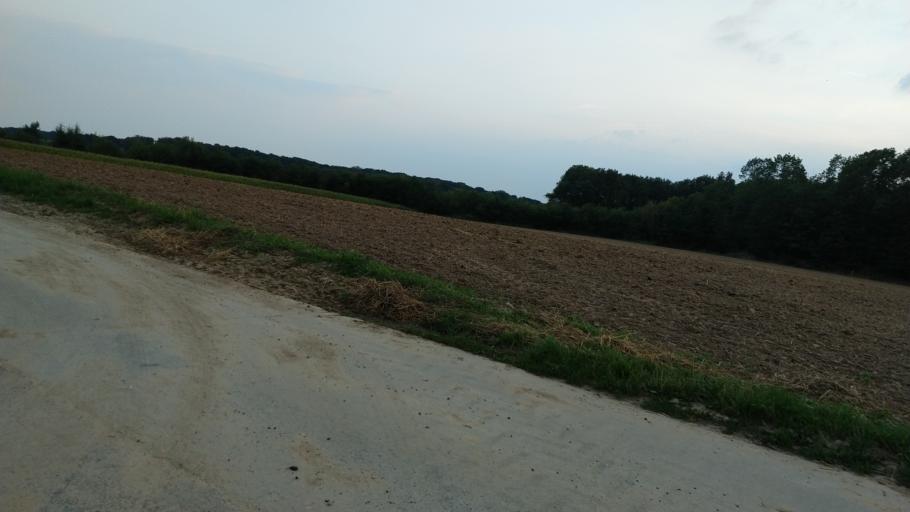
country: BE
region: Flanders
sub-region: Provincie Vlaams-Brabant
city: Boutersem
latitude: 50.8440
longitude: 4.8135
